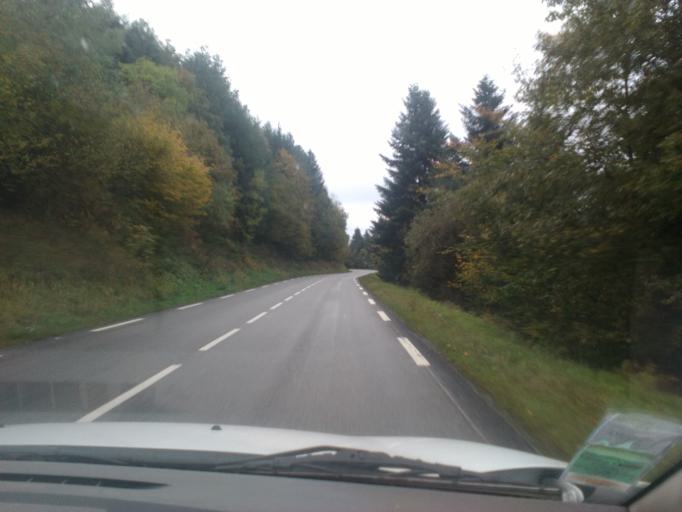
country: FR
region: Lorraine
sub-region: Departement des Vosges
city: Xonrupt-Longemer
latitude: 48.1291
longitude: 6.9161
